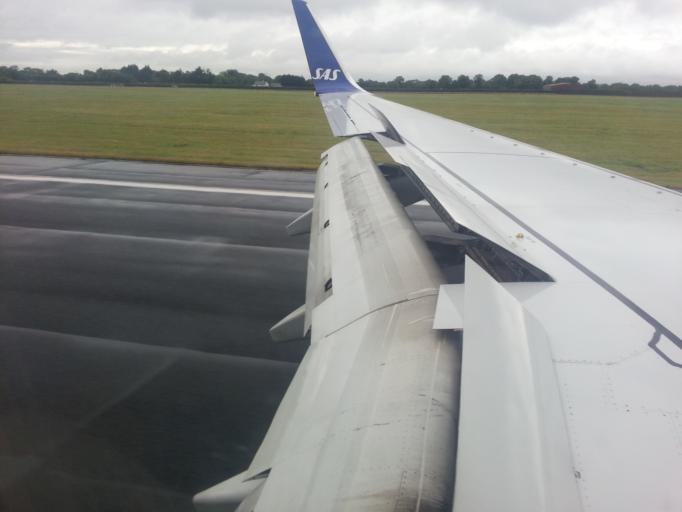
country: IE
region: Leinster
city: Ballymun
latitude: 53.4217
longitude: -6.2759
